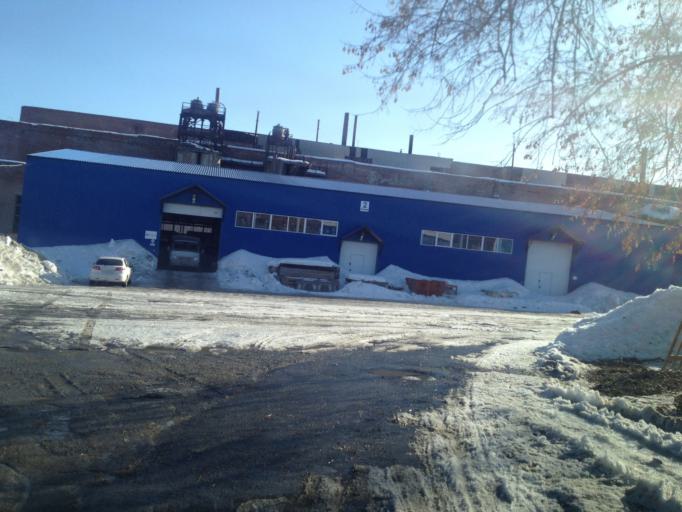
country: RU
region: Sverdlovsk
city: Yekaterinburg
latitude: 56.9116
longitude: 60.6387
